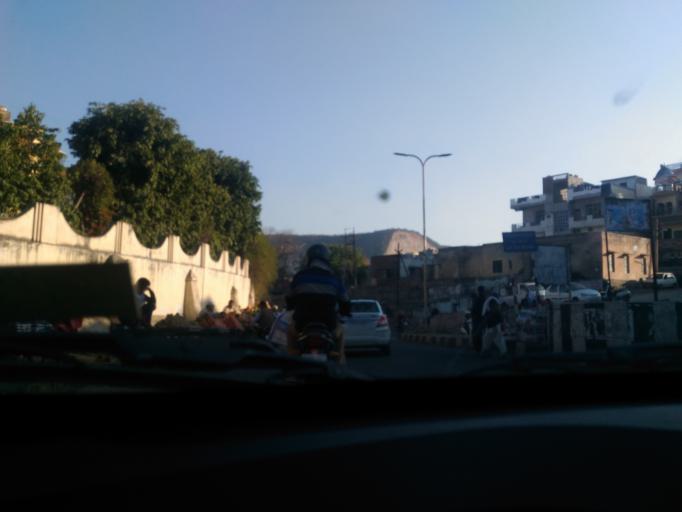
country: IN
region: Rajasthan
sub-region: Jaipur
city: Jaipur
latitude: 26.9029
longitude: 75.8458
